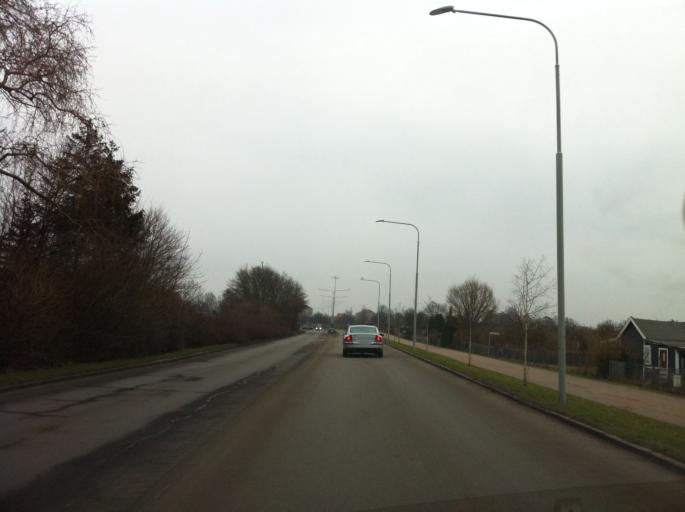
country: SE
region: Skane
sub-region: Landskrona
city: Landskrona
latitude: 55.8875
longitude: 12.8225
